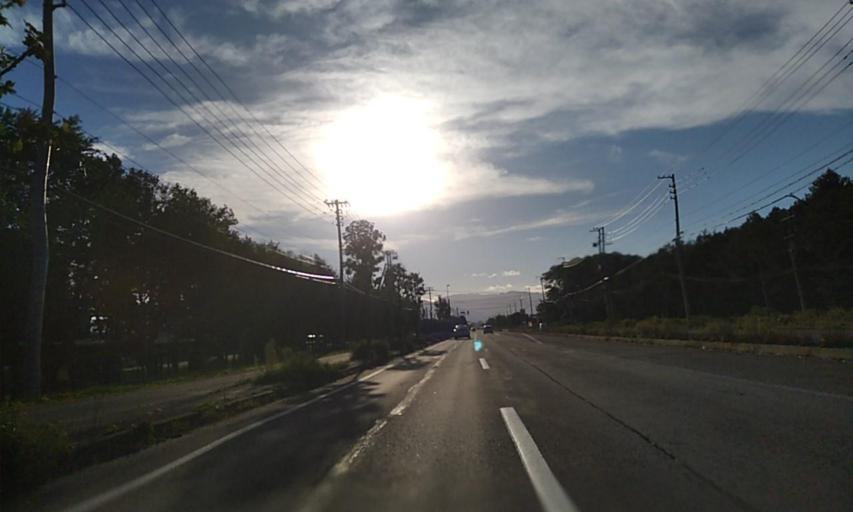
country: JP
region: Hokkaido
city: Obihiro
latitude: 42.9227
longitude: 143.0770
